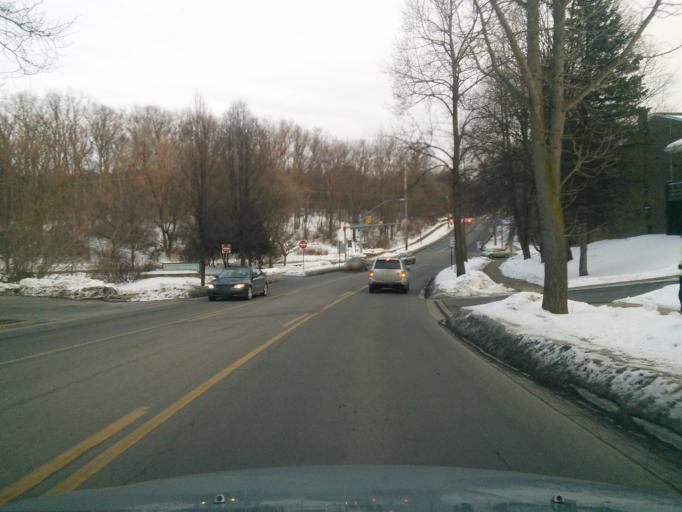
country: US
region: Pennsylvania
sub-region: Centre County
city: State College
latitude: 40.7970
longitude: -77.8438
